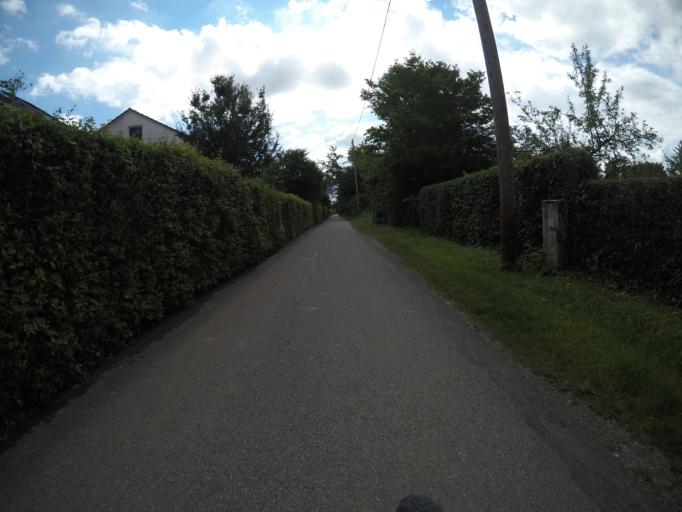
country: DE
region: Baden-Wuerttemberg
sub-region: Regierungsbezirk Stuttgart
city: Esslingen
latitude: 48.7246
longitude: 9.2811
